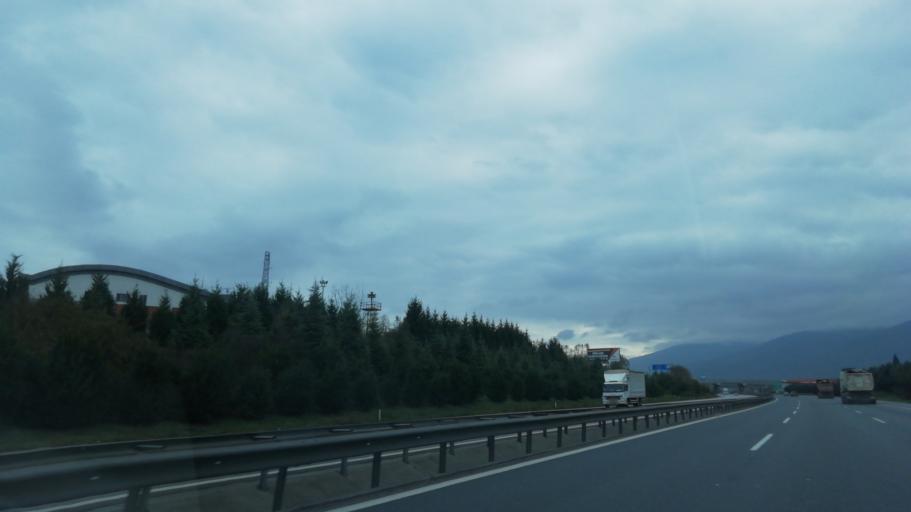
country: TR
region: Kocaeli
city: Kosekoy
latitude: 40.7356
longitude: 30.0509
